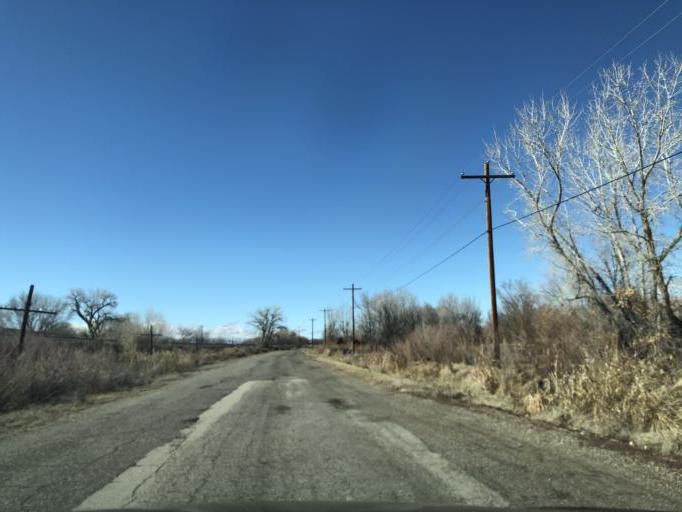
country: US
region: Utah
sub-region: Carbon County
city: East Carbon City
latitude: 38.9859
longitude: -110.1543
